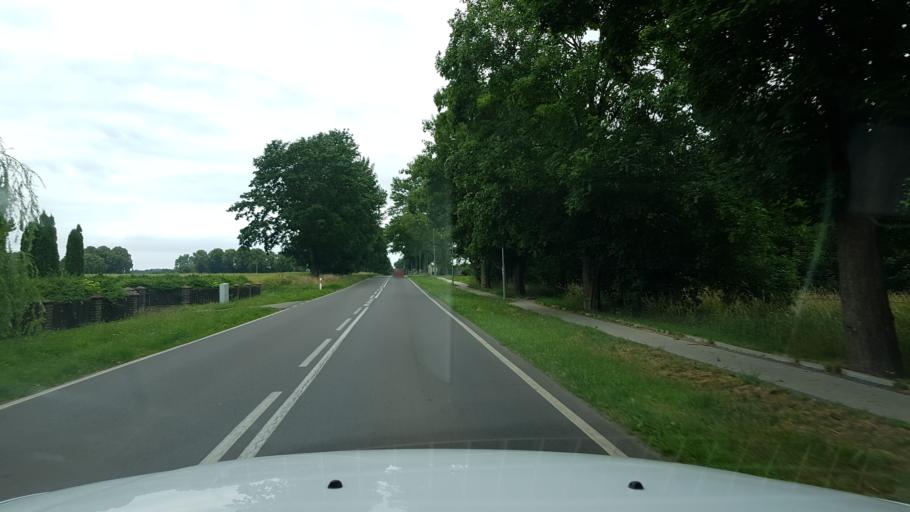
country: PL
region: West Pomeranian Voivodeship
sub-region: Powiat gryficki
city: Brojce
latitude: 53.9582
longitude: 15.3379
